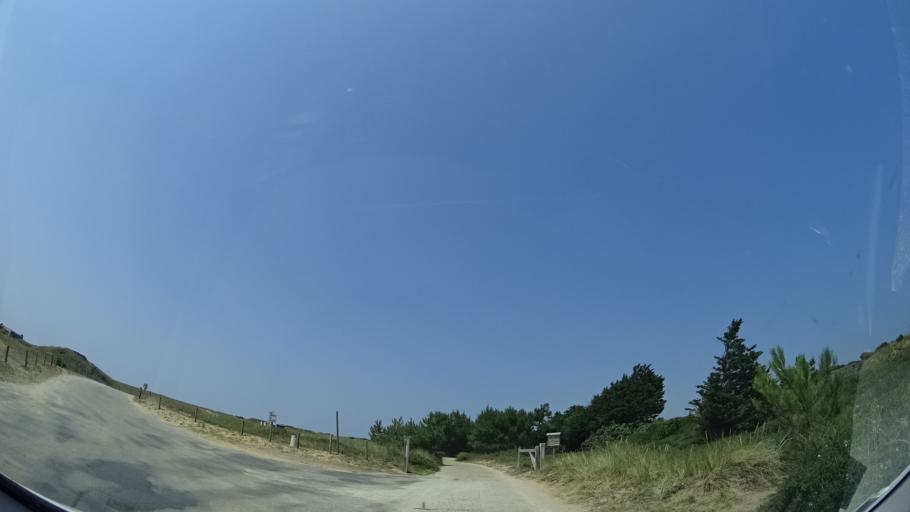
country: FR
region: Brittany
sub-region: Departement du Morbihan
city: Plouharnel
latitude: 47.5957
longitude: -3.1397
